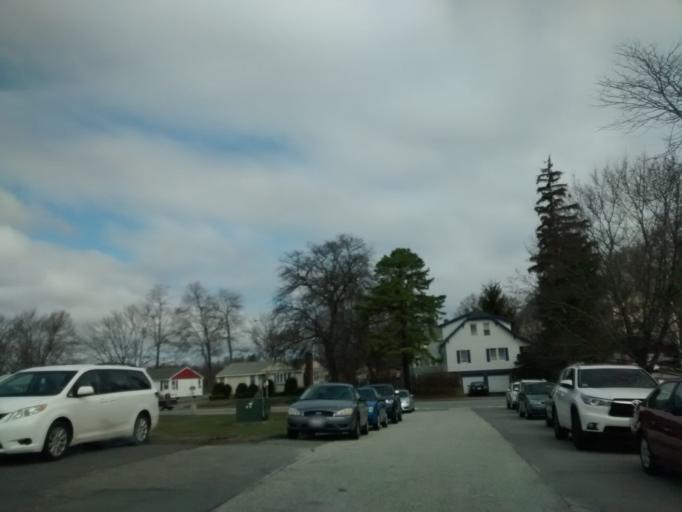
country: US
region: Massachusetts
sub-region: Worcester County
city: Worcester
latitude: 42.2890
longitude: -71.8120
